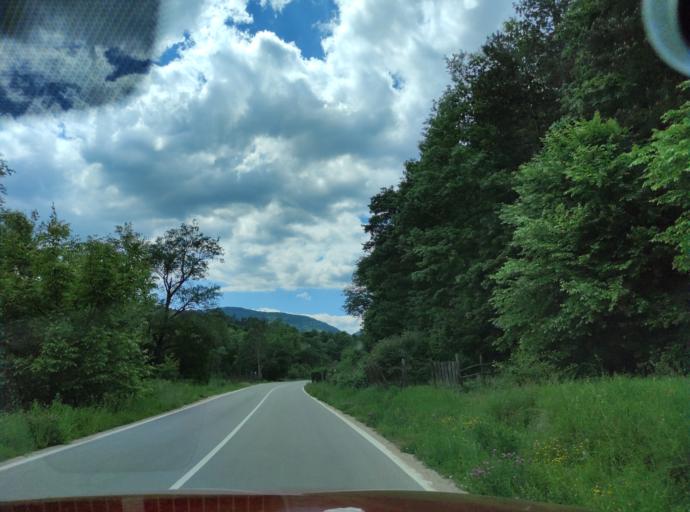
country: BG
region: Montana
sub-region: Obshtina Chiprovtsi
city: Chiprovtsi
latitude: 43.4664
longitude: 22.8716
